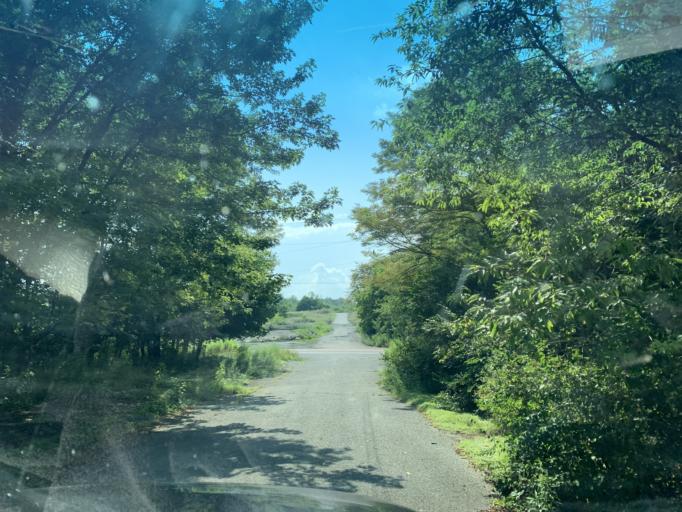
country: US
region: Pennsylvania
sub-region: Schuylkill County
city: Ashland
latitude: 40.8012
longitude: -76.3398
